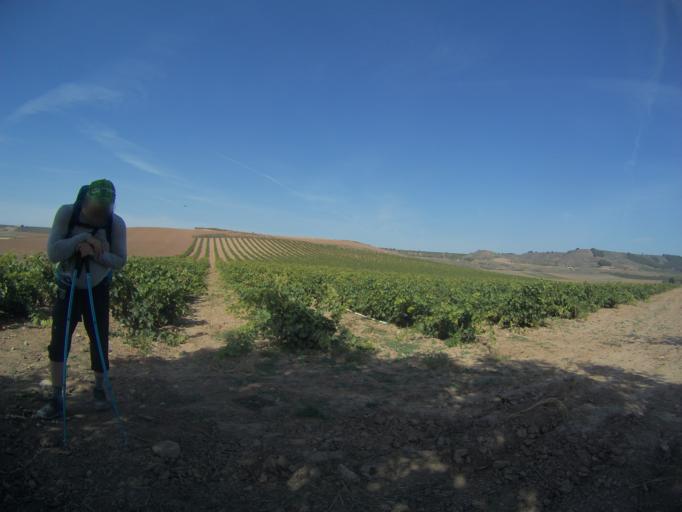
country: ES
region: La Rioja
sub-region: Provincia de La Rioja
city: Torrecilla sobre Alesanco
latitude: 42.4279
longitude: -2.8594
